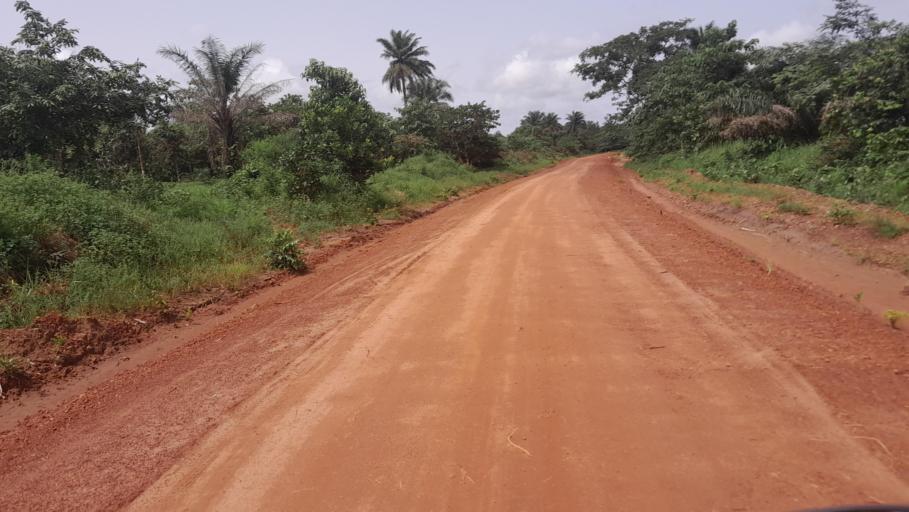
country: GN
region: Boke
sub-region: Boffa
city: Boffa
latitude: 10.0369
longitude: -13.8747
